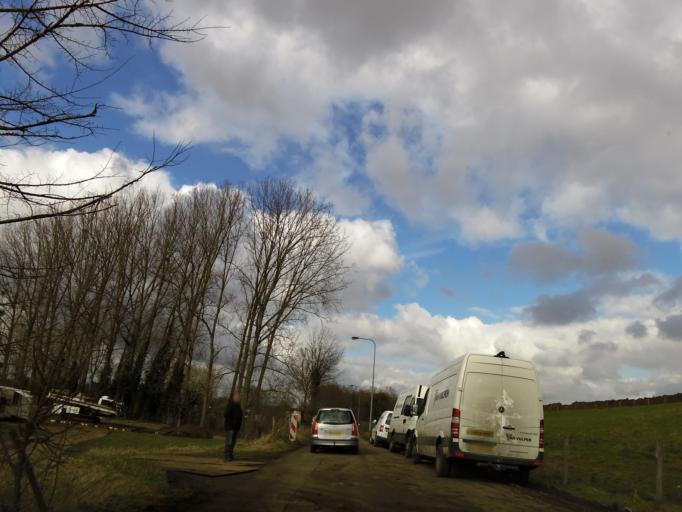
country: NL
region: Limburg
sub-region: Gemeente Stein
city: Stein
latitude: 50.9610
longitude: 5.7518
